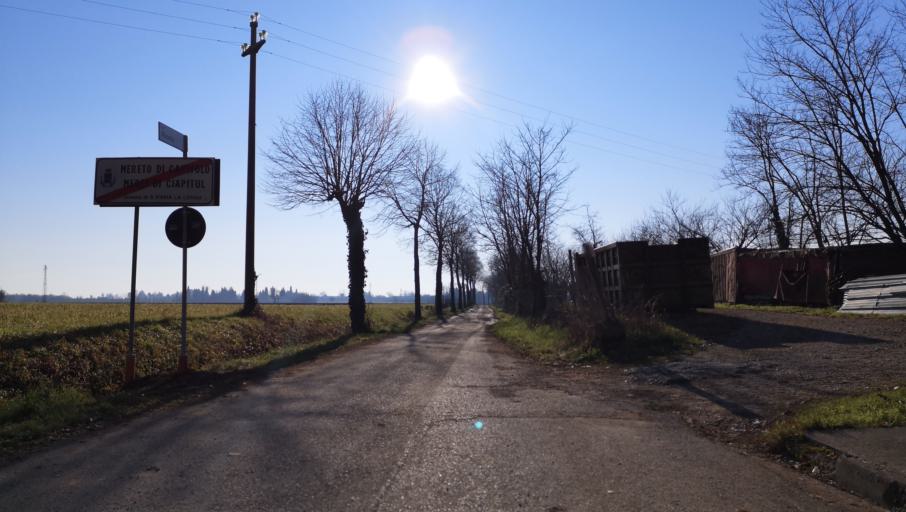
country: IT
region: Friuli Venezia Giulia
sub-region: Provincia di Udine
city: Santa Maria la Longa
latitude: 45.9193
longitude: 13.2974
